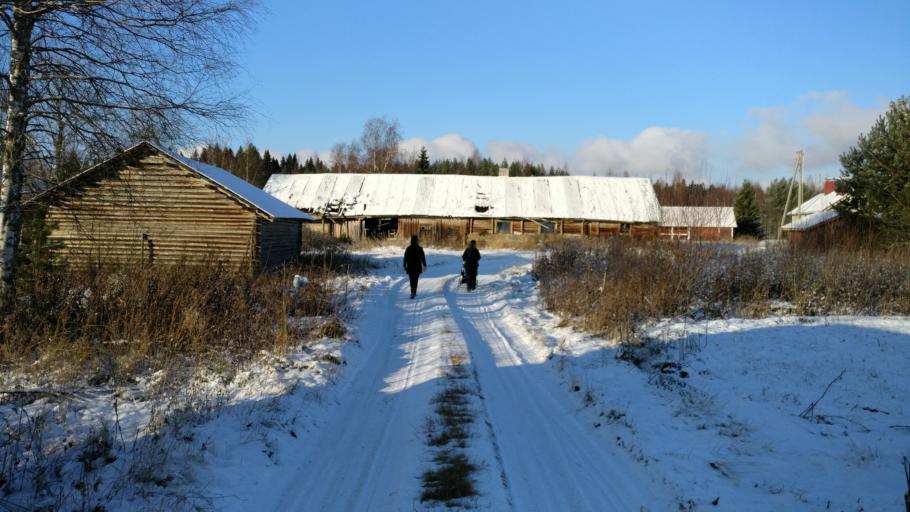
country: FI
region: Central Finland
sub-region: Jyvaeskylae
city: Hankasalmi
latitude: 62.4254
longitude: 26.6715
